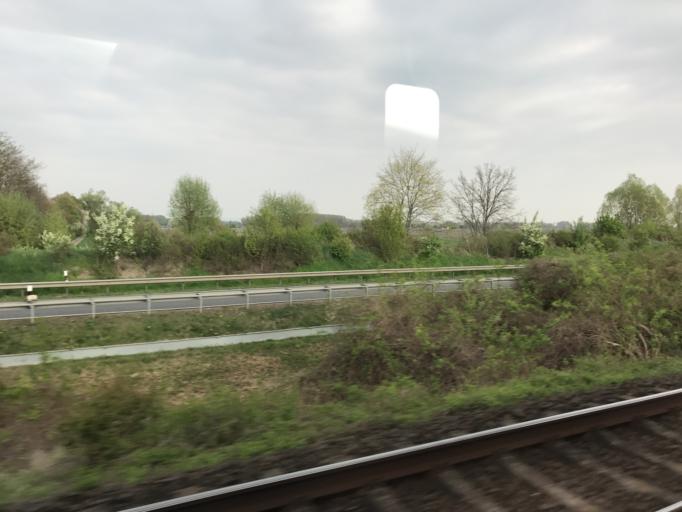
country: DE
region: Rheinland-Pfalz
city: Ludwigshohe
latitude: 49.8209
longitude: 8.3529
